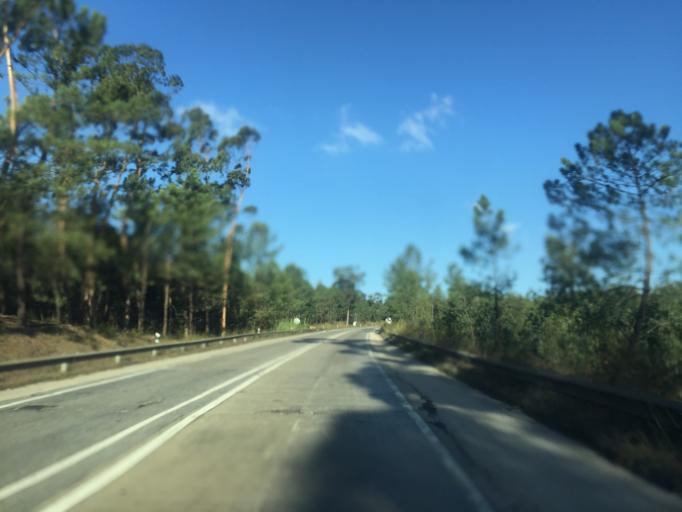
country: PT
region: Santarem
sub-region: Rio Maior
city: Rio Maior
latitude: 39.3264
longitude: -8.9551
